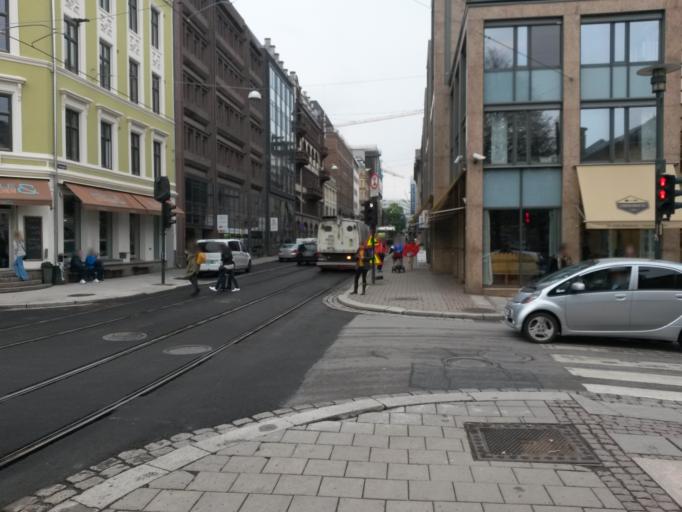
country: NO
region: Oslo
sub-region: Oslo
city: Oslo
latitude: 59.9103
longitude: 10.7387
